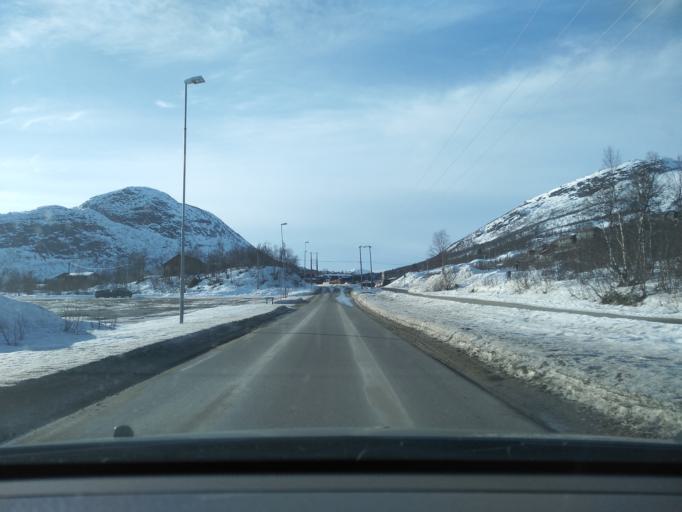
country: NO
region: Aust-Agder
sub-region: Bykle
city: Hovden
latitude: 59.5688
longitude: 7.3550
